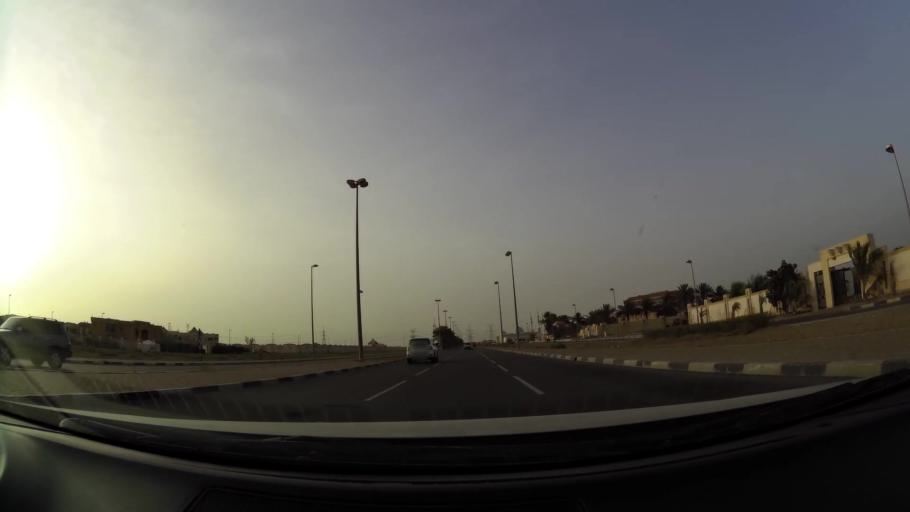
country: OM
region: Al Buraimi
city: Al Buraymi
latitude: 24.2677
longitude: 55.7205
